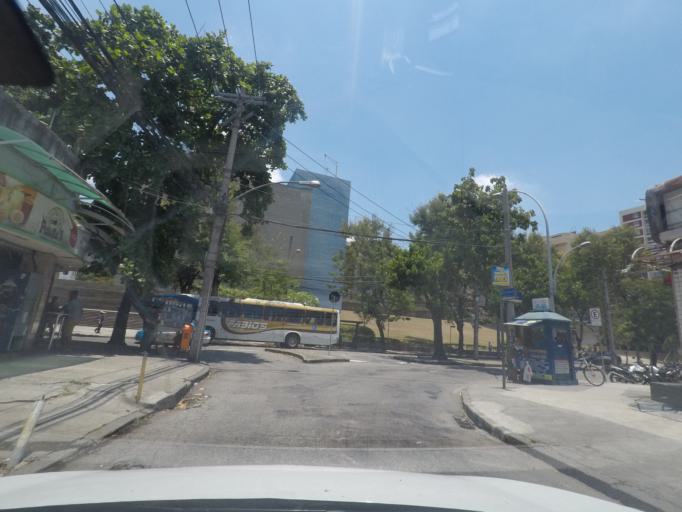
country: BR
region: Rio de Janeiro
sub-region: Rio De Janeiro
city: Rio de Janeiro
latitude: -22.9213
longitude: -43.2502
